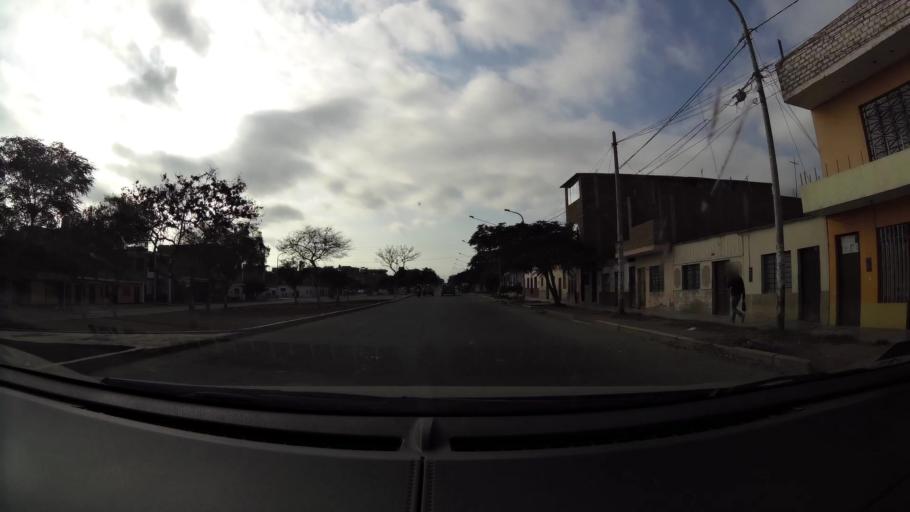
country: PE
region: La Libertad
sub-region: Provincia de Trujillo
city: La Esperanza
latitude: -8.0814
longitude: -79.0423
